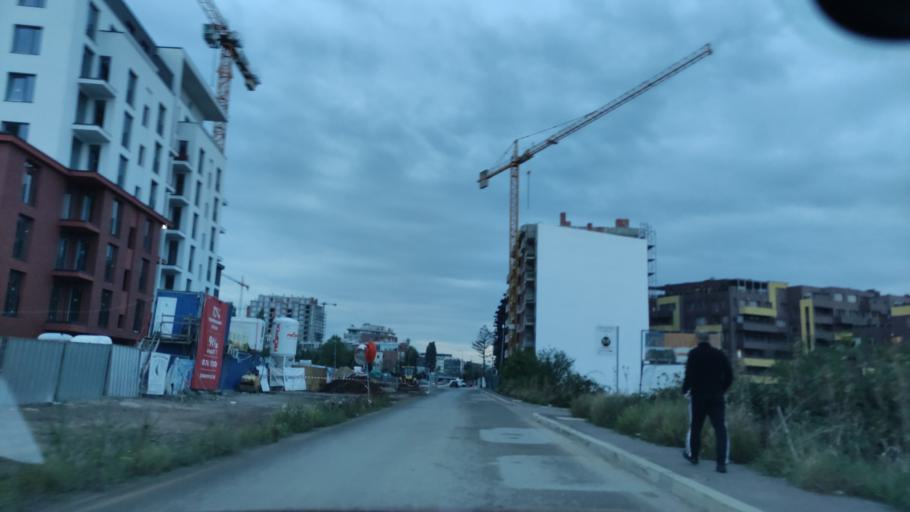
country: BG
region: Sofia-Capital
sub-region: Stolichna Obshtina
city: Sofia
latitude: 42.6551
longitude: 23.2898
